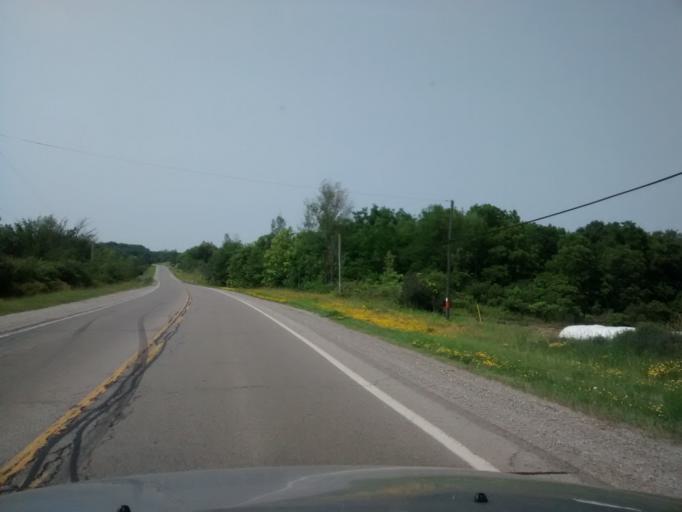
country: CA
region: Ontario
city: Ancaster
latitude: 42.9940
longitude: -79.8657
